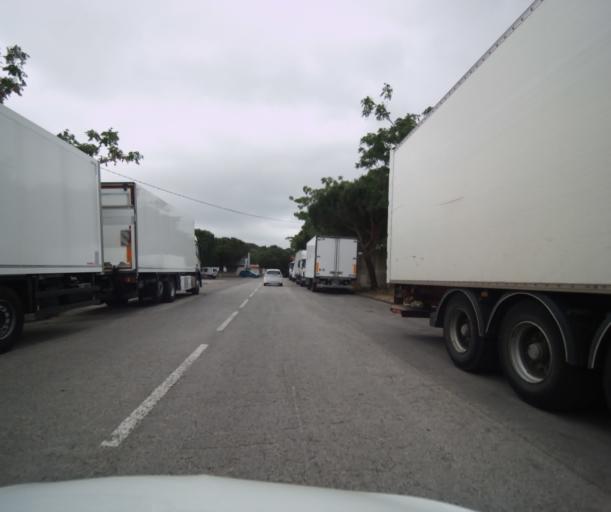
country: FR
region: Provence-Alpes-Cote d'Azur
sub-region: Departement du Var
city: La Seyne-sur-Mer
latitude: 43.1222
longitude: 5.8927
